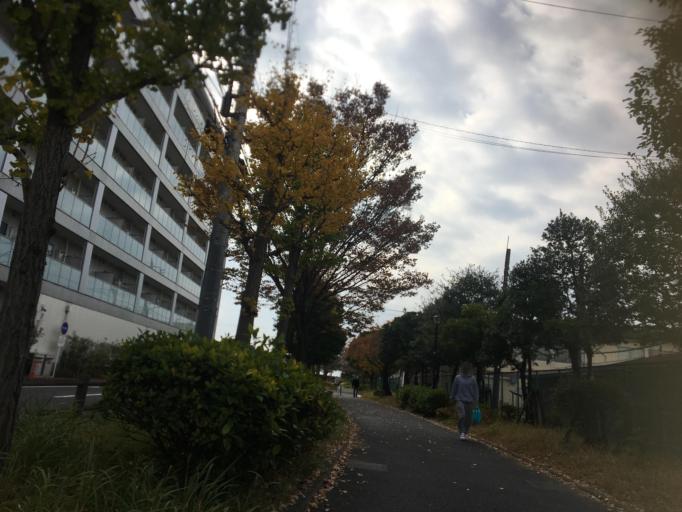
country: JP
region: Tokyo
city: Urayasu
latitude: 35.6512
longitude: 139.8835
